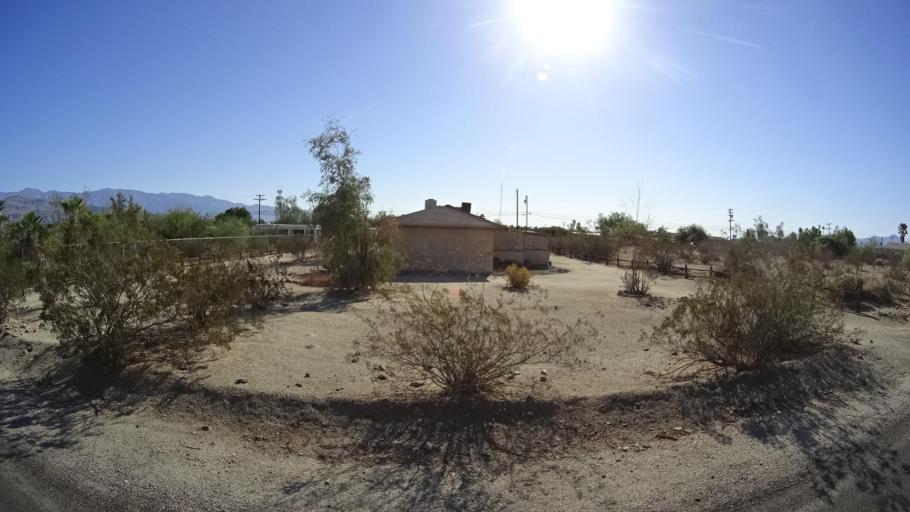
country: US
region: California
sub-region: San Diego County
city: Borrego Springs
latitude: 33.2602
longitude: -116.3749
